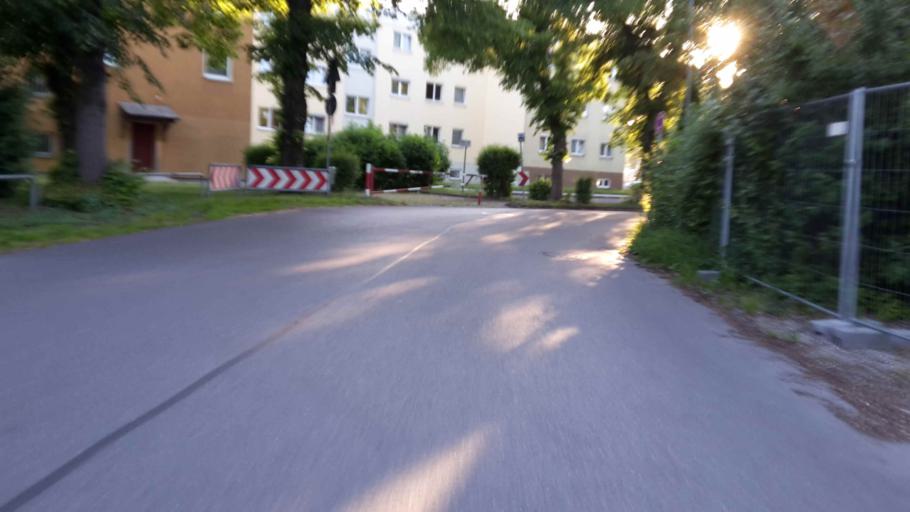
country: DE
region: Bavaria
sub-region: Upper Bavaria
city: Karlsfeld
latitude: 48.2184
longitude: 11.4821
